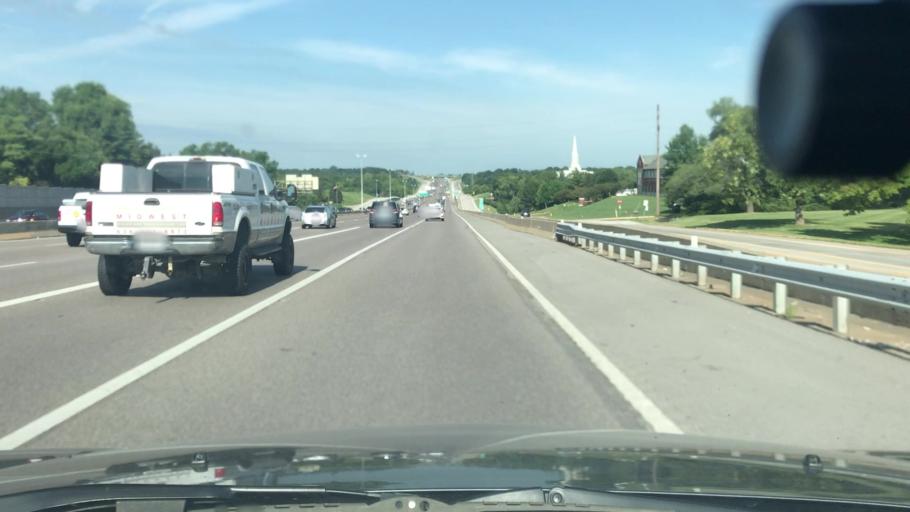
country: US
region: Missouri
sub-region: Saint Louis County
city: Town and Country
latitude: 38.6388
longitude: -90.4565
